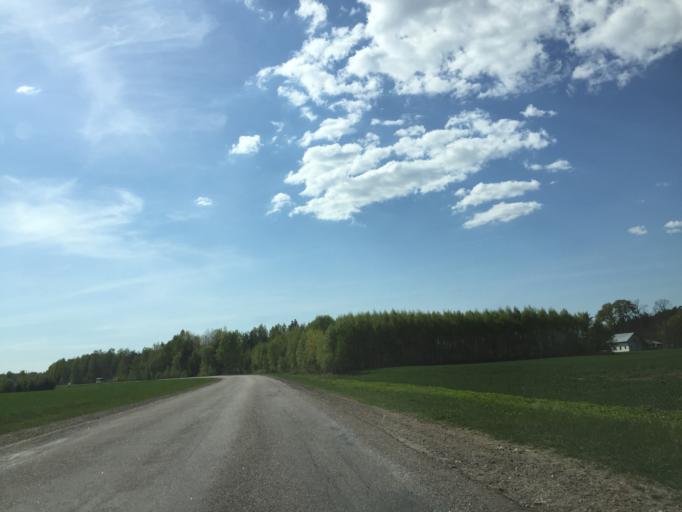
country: LV
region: Limbazu Rajons
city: Limbazi
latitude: 57.5139
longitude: 24.7802
